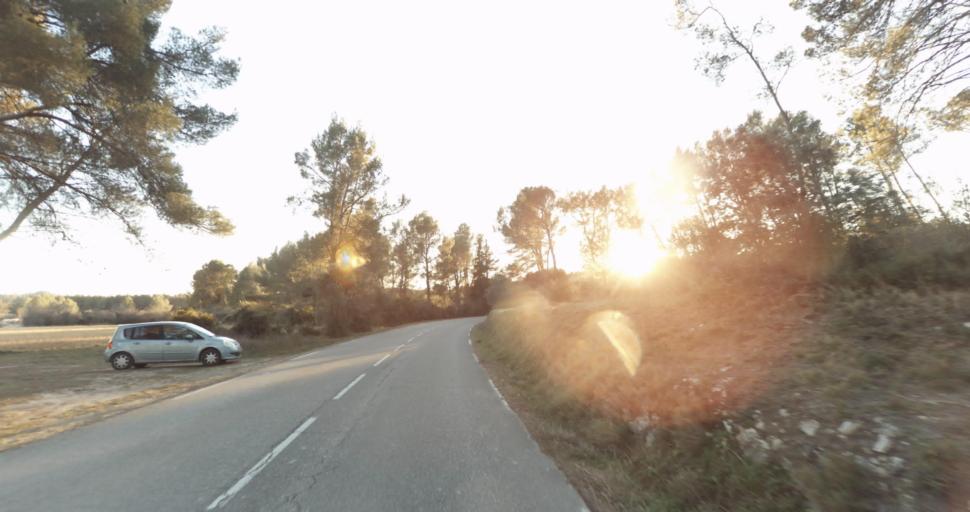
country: FR
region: Provence-Alpes-Cote d'Azur
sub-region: Departement des Bouches-du-Rhone
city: Barbentane
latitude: 43.8898
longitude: 4.7416
